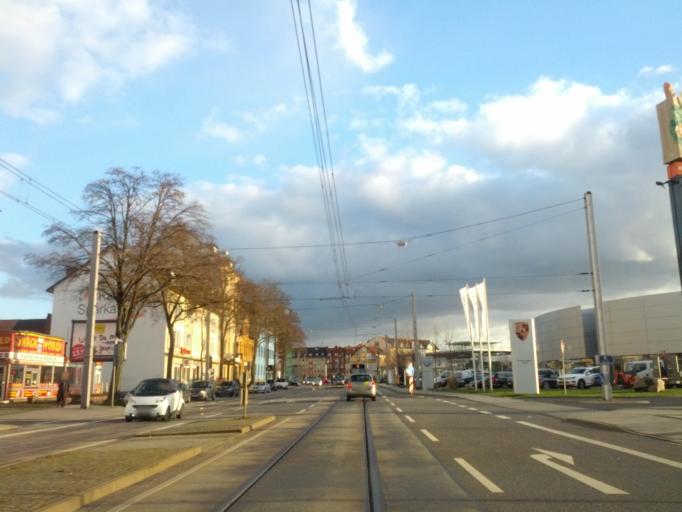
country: DE
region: Hesse
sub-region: Regierungsbezirk Kassel
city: Kassel
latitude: 51.3055
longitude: 9.5280
